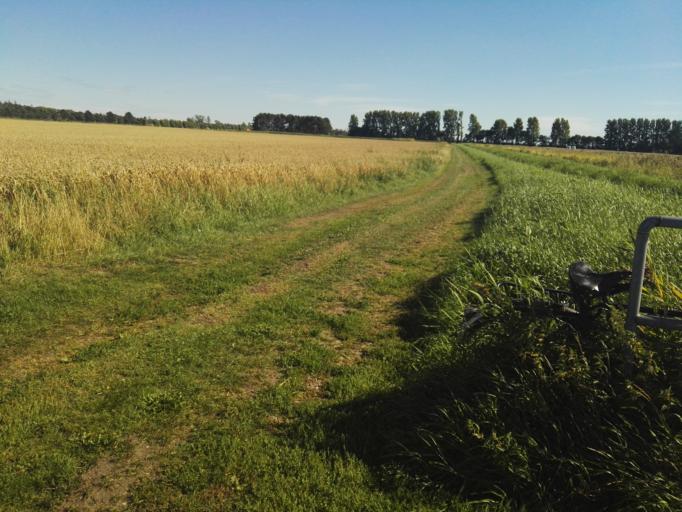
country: DK
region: Zealand
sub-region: Odsherred Kommune
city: Nykobing Sjaelland
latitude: 55.9251
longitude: 11.6888
